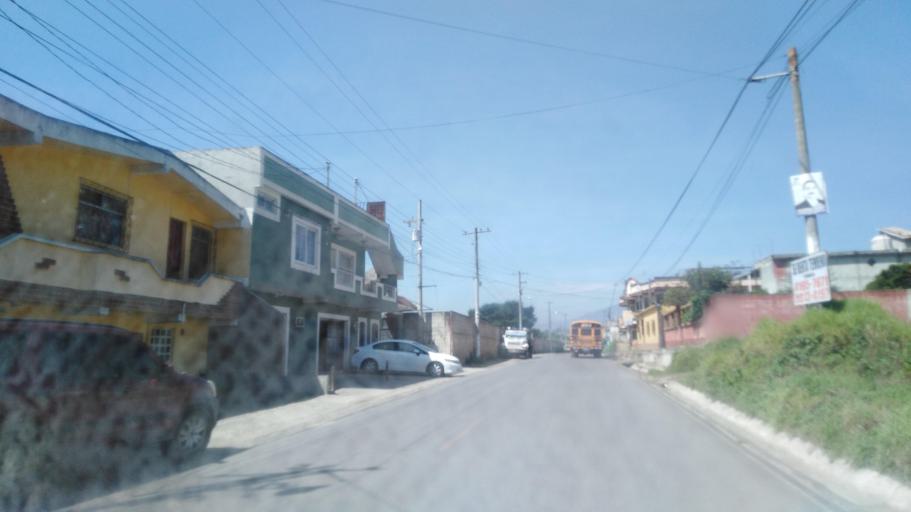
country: GT
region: Quetzaltenango
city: Quetzaltenango
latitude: 14.8541
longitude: -91.4924
